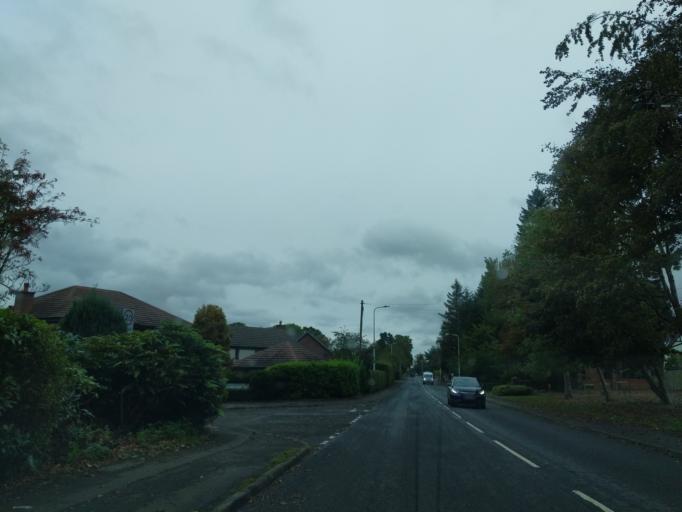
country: GB
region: Scotland
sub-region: Edinburgh
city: Balerno
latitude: 55.8811
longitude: -3.3489
